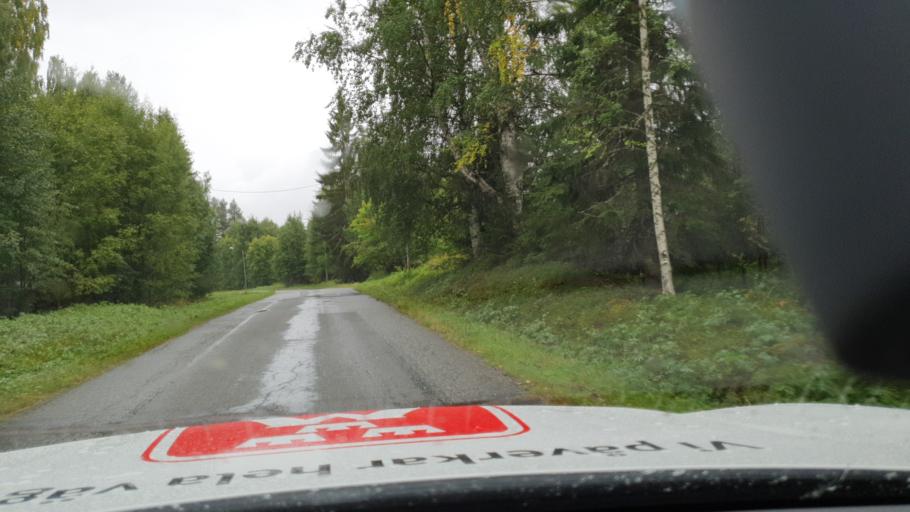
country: SE
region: Vaesterbotten
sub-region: Dorotea Kommun
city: Dorotea
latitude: 64.1146
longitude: 16.3199
